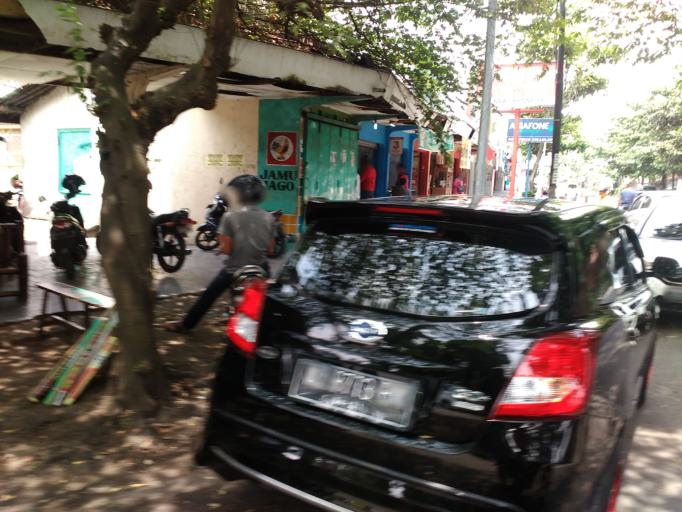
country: ID
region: Central Java
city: Boyolali
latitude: -7.5441
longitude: 110.6019
